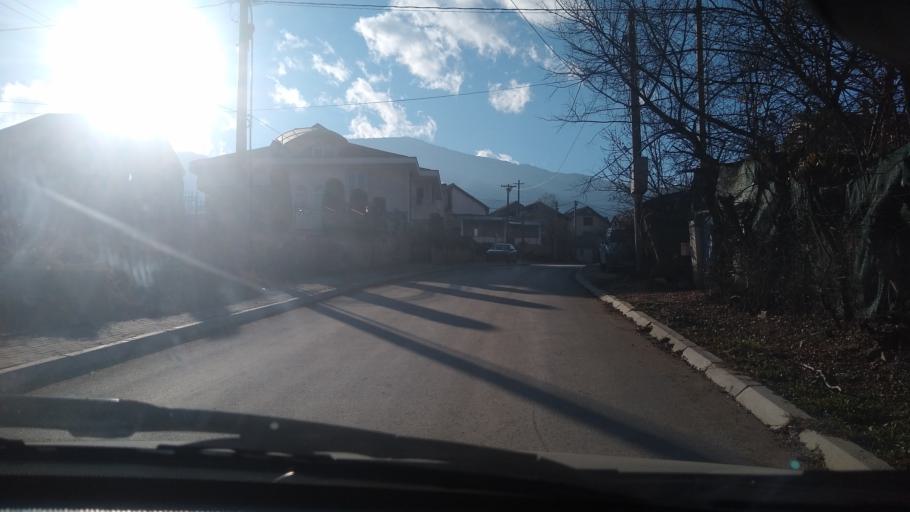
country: MK
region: Bitola
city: Bitola
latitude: 41.0192
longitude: 21.3147
